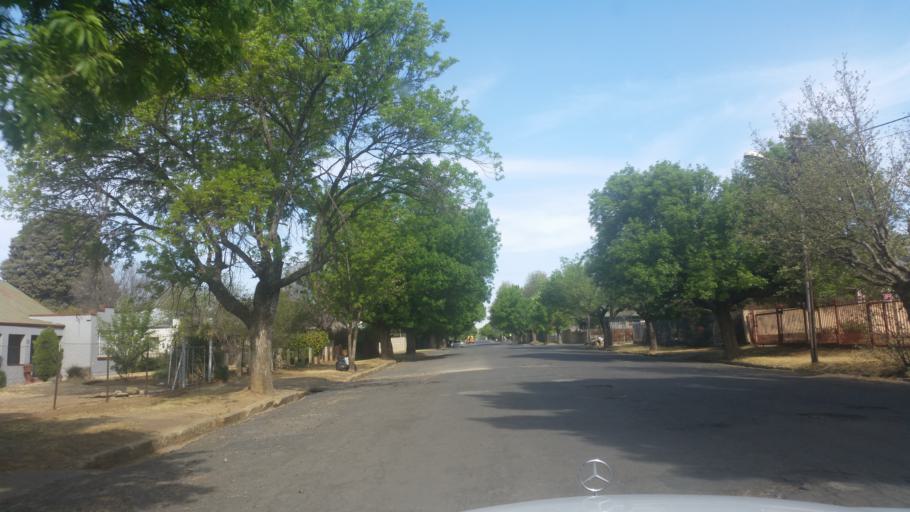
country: ZA
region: Orange Free State
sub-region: Thabo Mofutsanyana District Municipality
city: Harrismith
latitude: -28.2661
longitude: 29.1234
